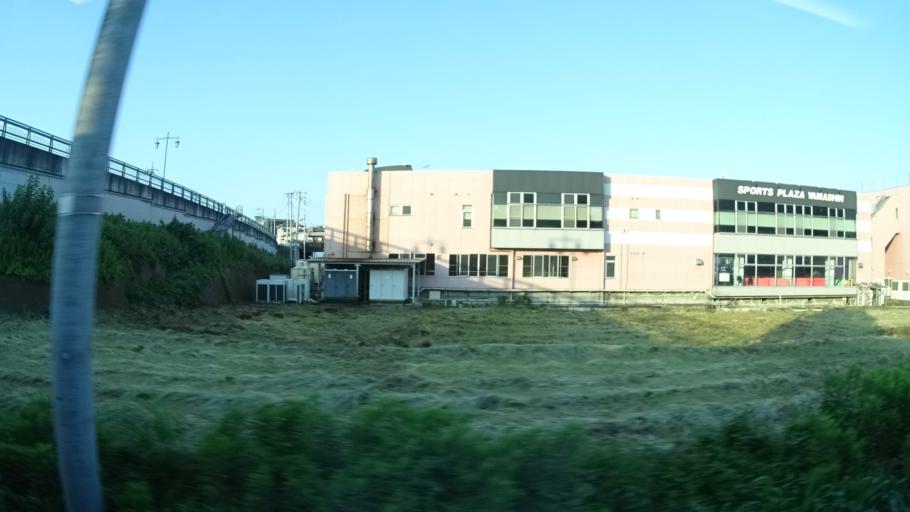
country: JP
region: Ibaraki
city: Ishioka
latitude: 36.1932
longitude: 140.2785
